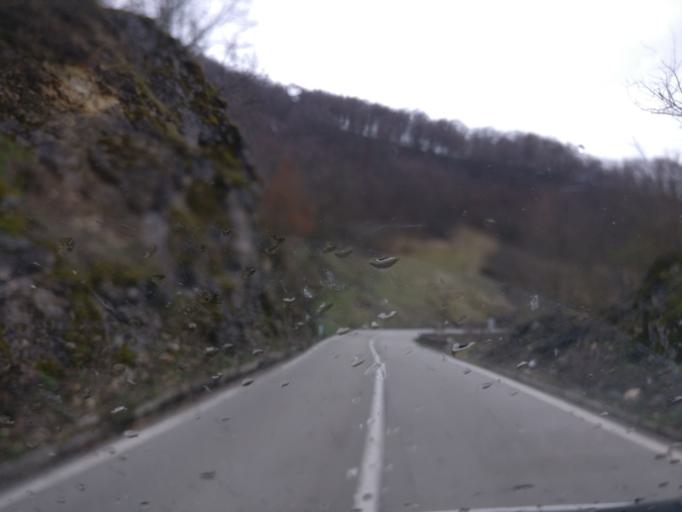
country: ME
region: Opstina Pluzine
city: Pluzine
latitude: 43.1467
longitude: 18.8342
